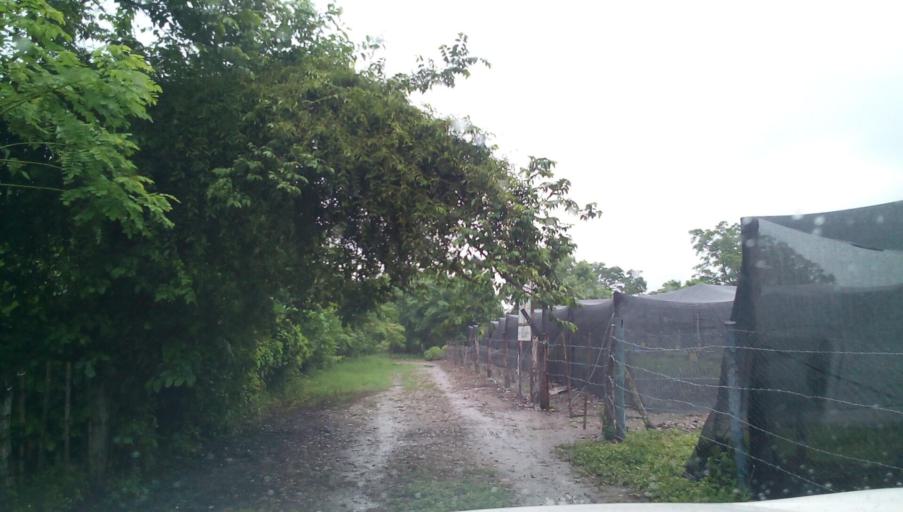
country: MX
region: Veracruz
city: Tempoal de Sanchez
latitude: 21.4162
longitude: -98.4233
